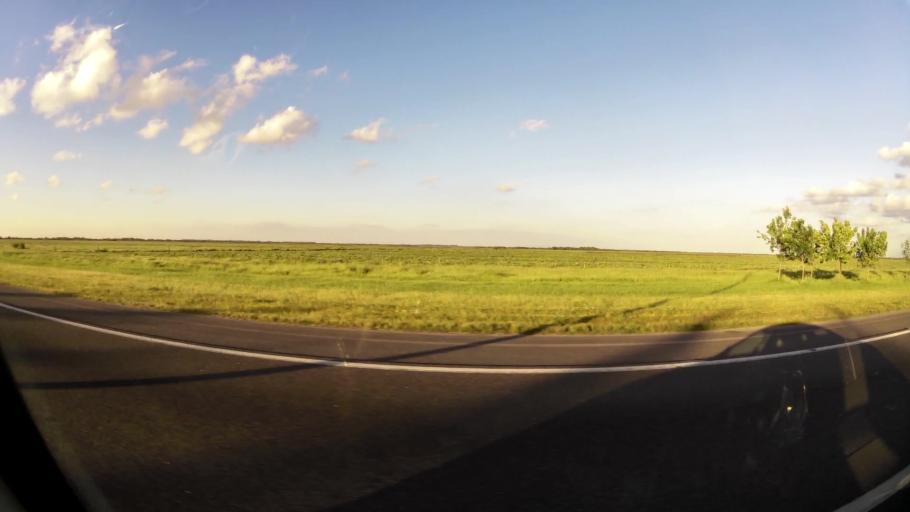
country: AR
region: Buenos Aires
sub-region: Partido de La Plata
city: La Plata
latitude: -34.8299
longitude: -58.0898
